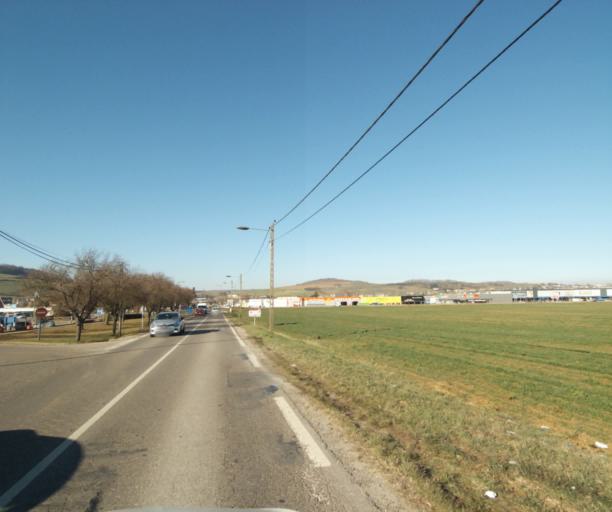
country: FR
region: Lorraine
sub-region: Departement de Meurthe-et-Moselle
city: Pulnoy
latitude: 48.7028
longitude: 6.2467
